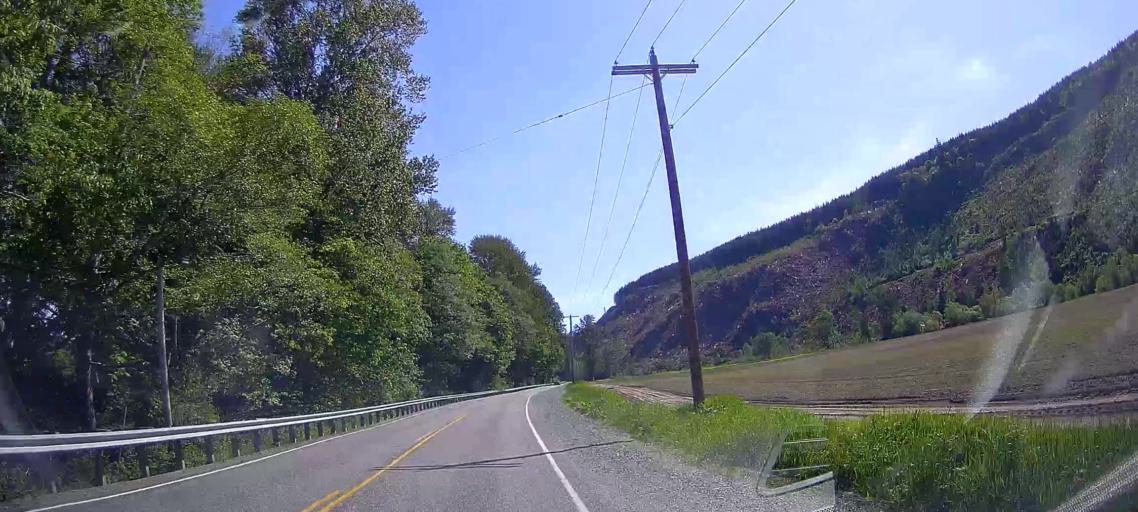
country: US
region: Washington
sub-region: Skagit County
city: Sedro-Woolley
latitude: 48.4866
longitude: -122.2312
